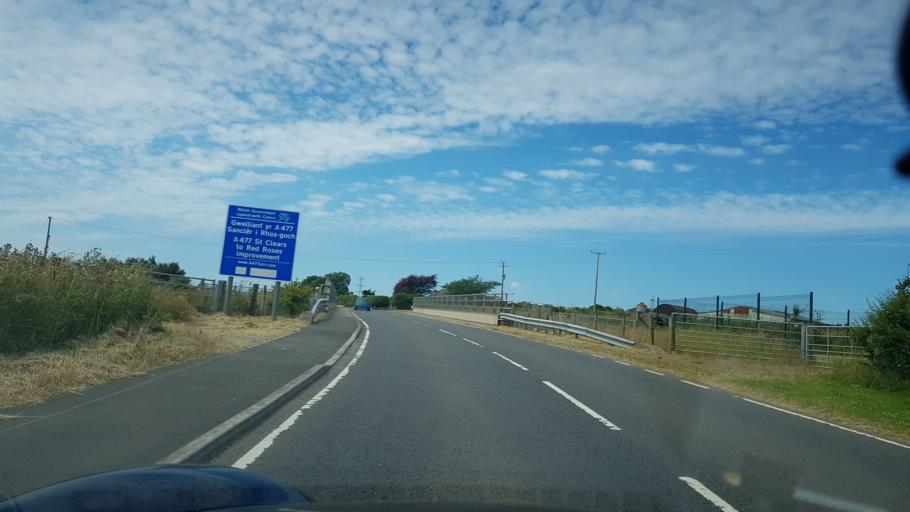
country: GB
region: Wales
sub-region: Carmarthenshire
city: Whitland
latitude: 51.7770
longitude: -4.6074
